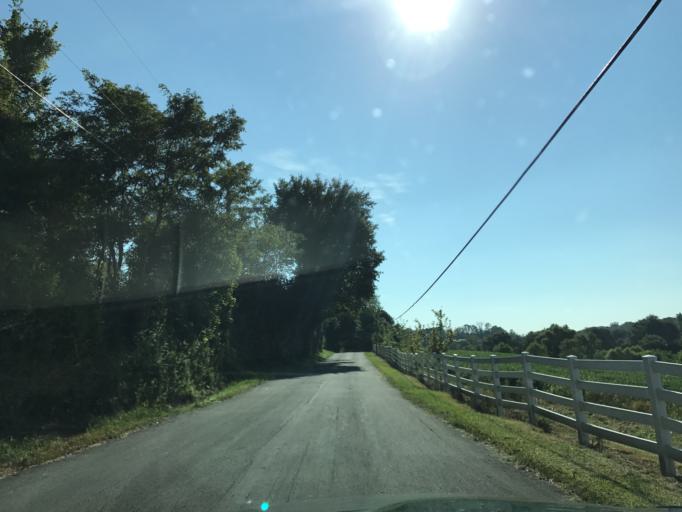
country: US
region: Pennsylvania
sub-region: York County
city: Stewartstown
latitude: 39.6461
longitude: -76.5885
